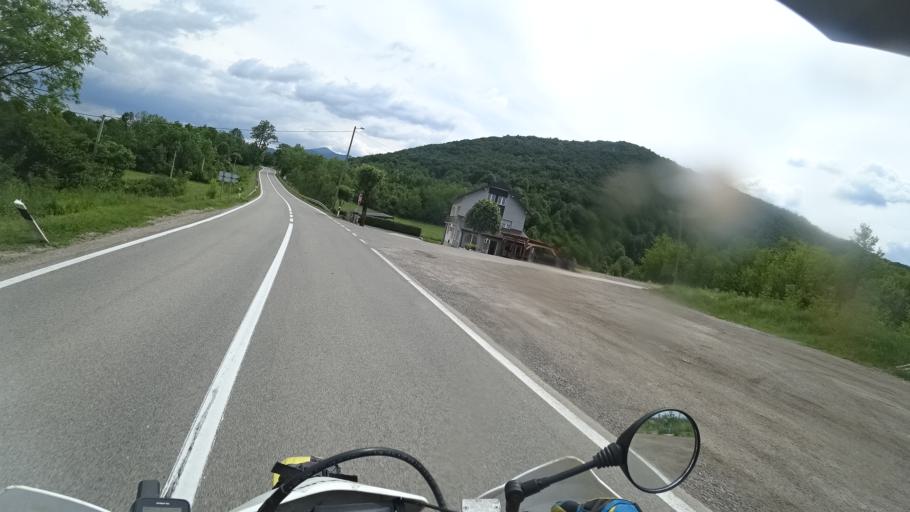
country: BA
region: Federation of Bosnia and Herzegovina
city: Izacic
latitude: 44.8911
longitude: 15.7243
